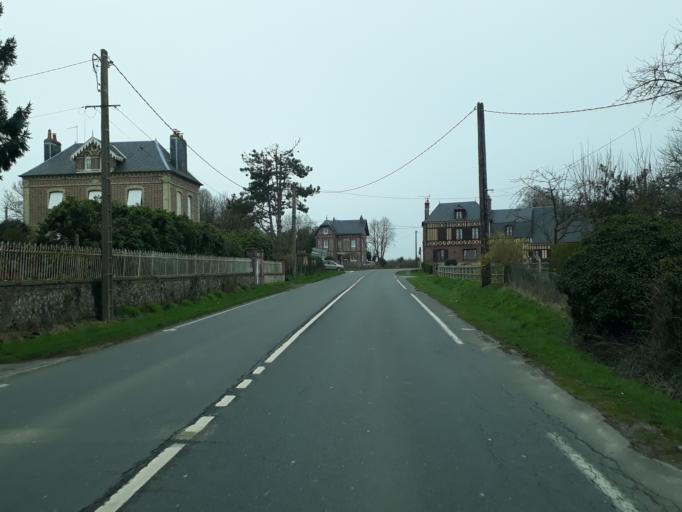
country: FR
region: Haute-Normandie
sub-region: Departement de la Seine-Maritime
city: Beuzeville-la-Grenier
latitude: 49.5954
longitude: 0.4221
